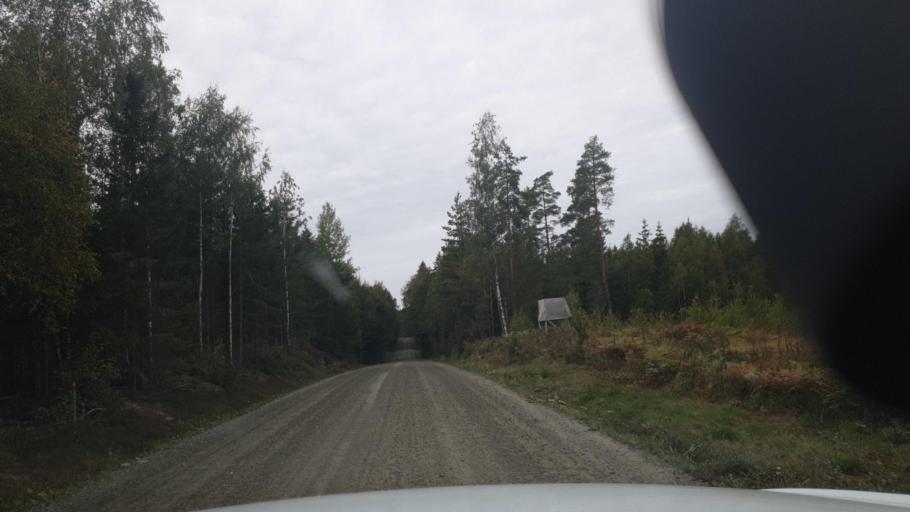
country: SE
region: Vaermland
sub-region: Karlstads Kommun
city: Valberg
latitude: 59.4495
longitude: 13.1075
